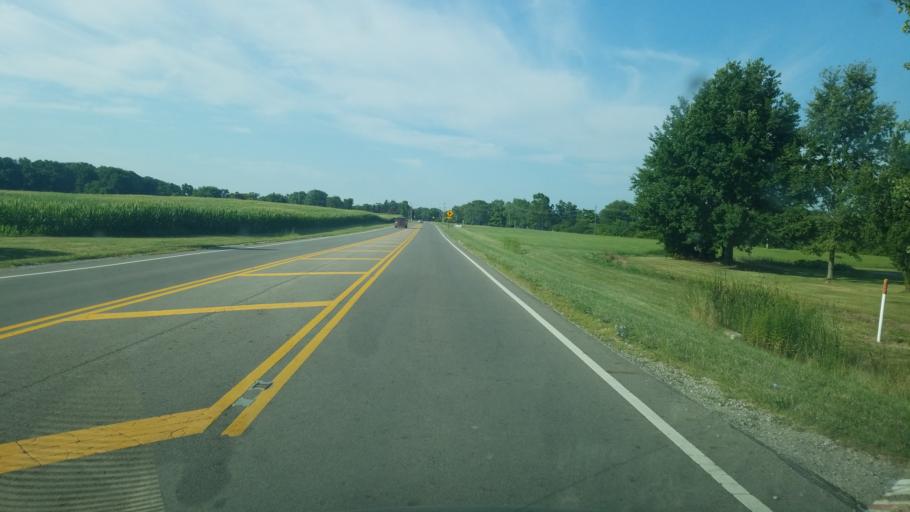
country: US
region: Ohio
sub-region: Franklin County
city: Lincoln Village
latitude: 39.9087
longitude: -83.1444
